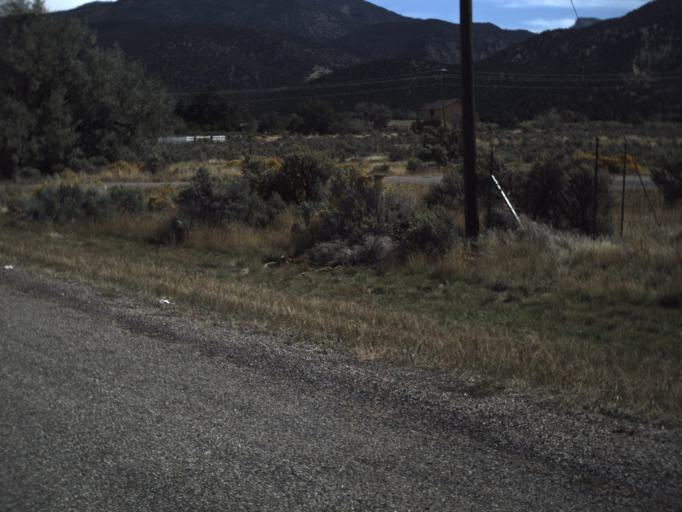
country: US
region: Utah
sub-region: Iron County
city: Enoch
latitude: 37.8010
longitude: -112.9427
